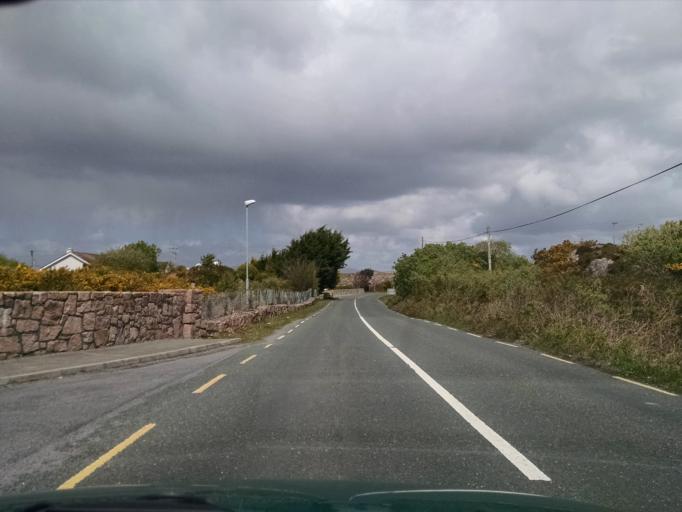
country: IE
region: Connaught
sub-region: County Galway
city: Oughterard
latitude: 53.2927
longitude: -9.5496
